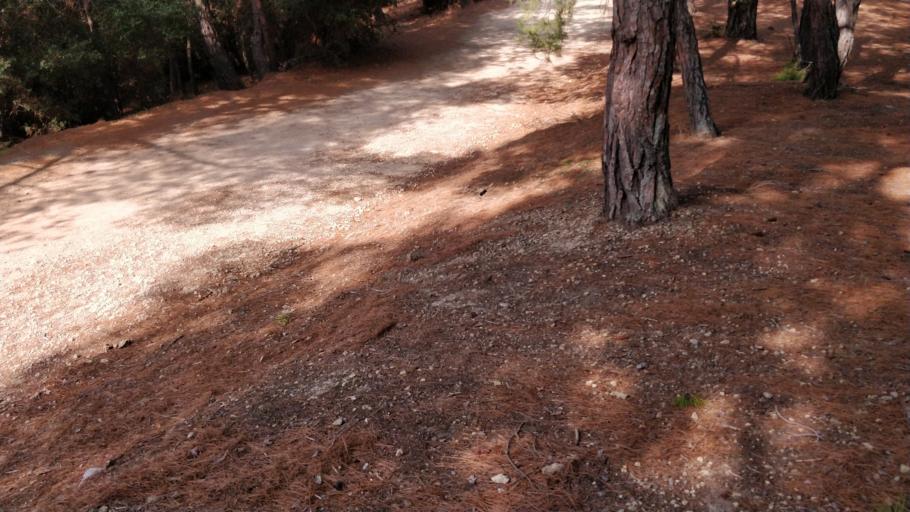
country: TR
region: Canakkale
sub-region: Merkez
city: Kucukkuyu
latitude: 39.5618
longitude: 26.6176
